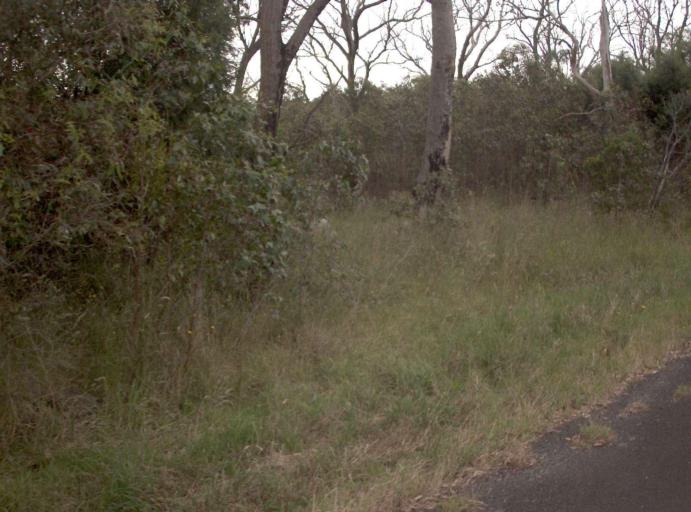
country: AU
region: Victoria
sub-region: Latrobe
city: Traralgon
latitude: -38.5585
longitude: 146.8082
